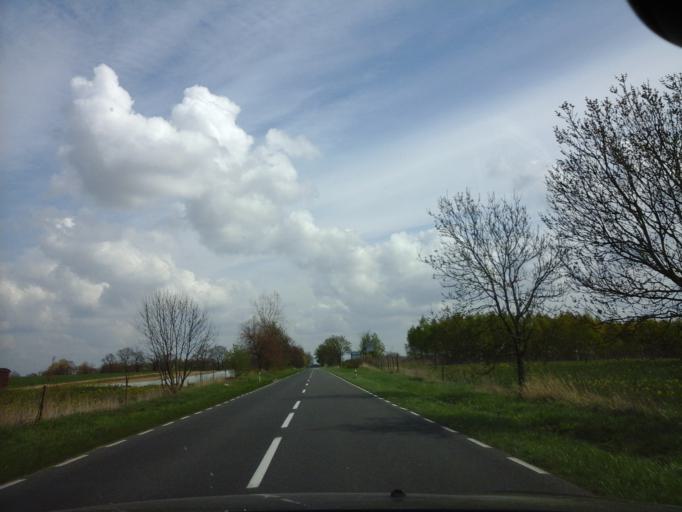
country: PL
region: West Pomeranian Voivodeship
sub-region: Powiat choszczenski
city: Choszczno
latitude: 53.1970
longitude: 15.3676
